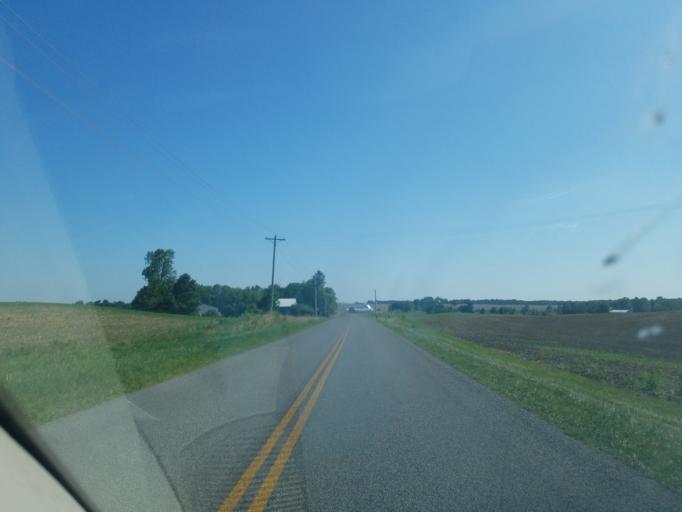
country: US
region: Ohio
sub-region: Logan County
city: Northwood
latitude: 40.4277
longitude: -83.6635
